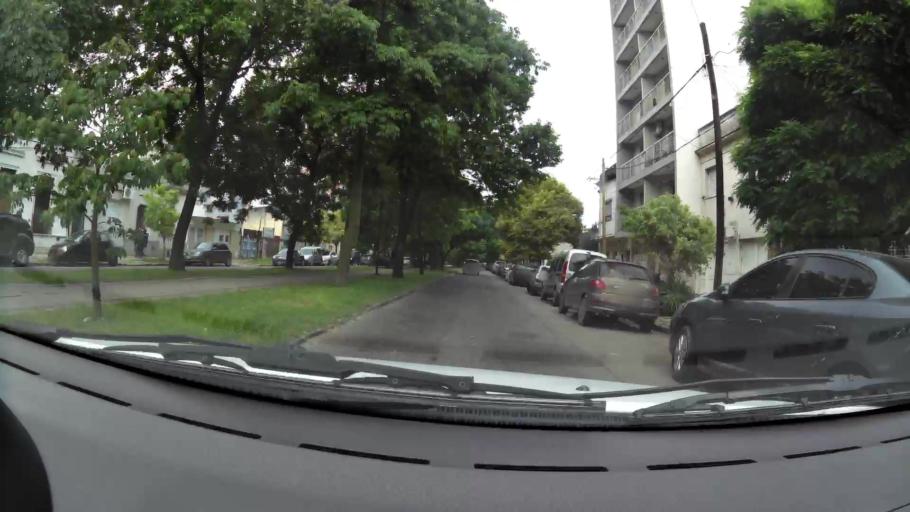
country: AR
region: Buenos Aires
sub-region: Partido de La Plata
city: La Plata
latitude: -34.9284
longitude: -57.9453
